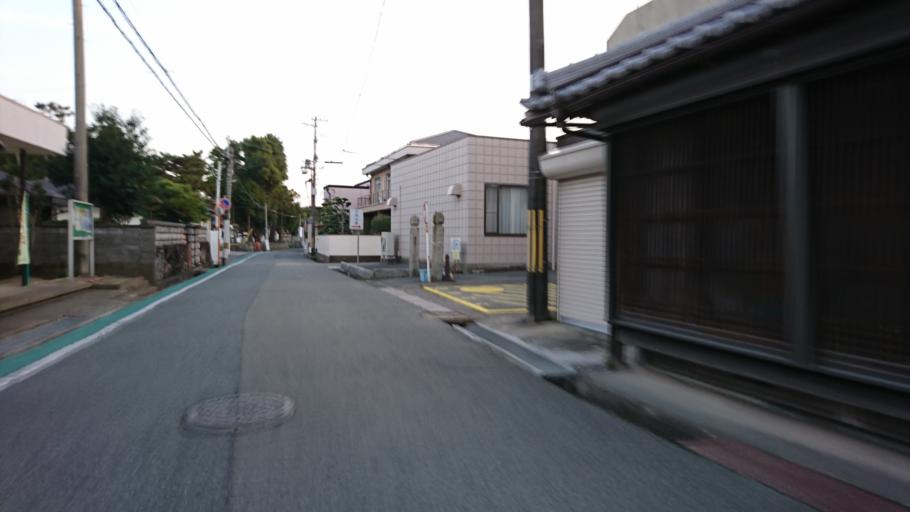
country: JP
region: Hyogo
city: Kakogawacho-honmachi
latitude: 34.7400
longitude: 134.8725
